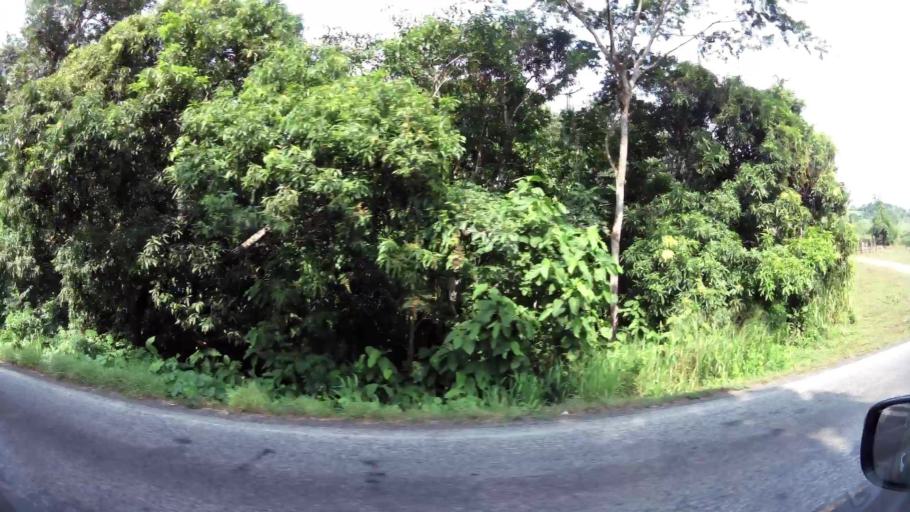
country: CR
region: Guanacaste
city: Juntas
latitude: 10.1769
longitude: -84.9299
